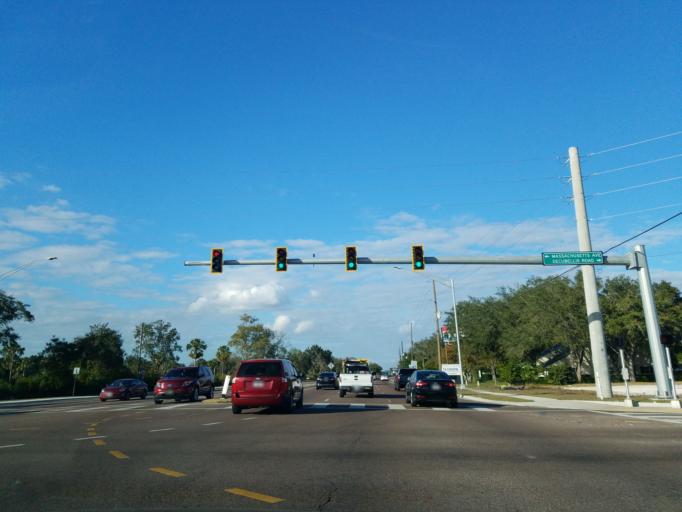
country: US
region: Florida
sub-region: Pasco County
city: New Port Richey East
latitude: 28.2587
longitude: -82.6743
